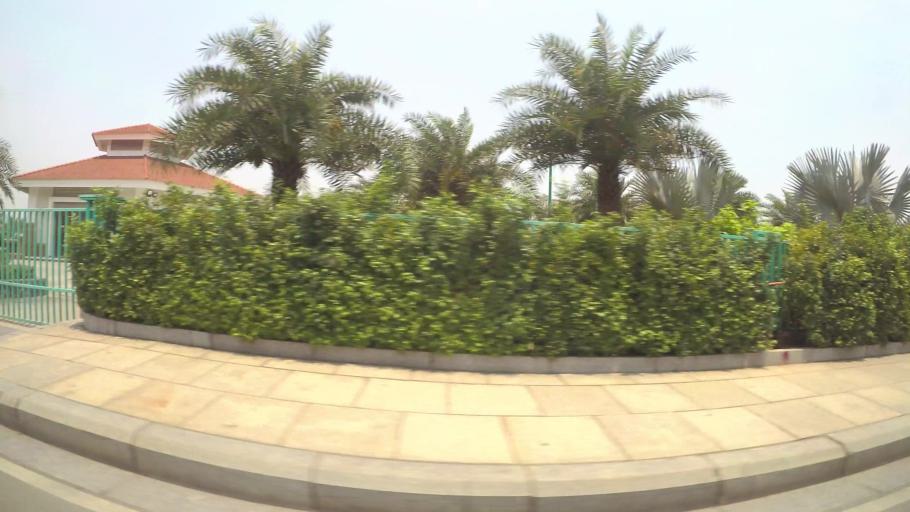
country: VN
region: Ha Noi
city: Trau Quy
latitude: 21.0385
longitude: 105.8959
